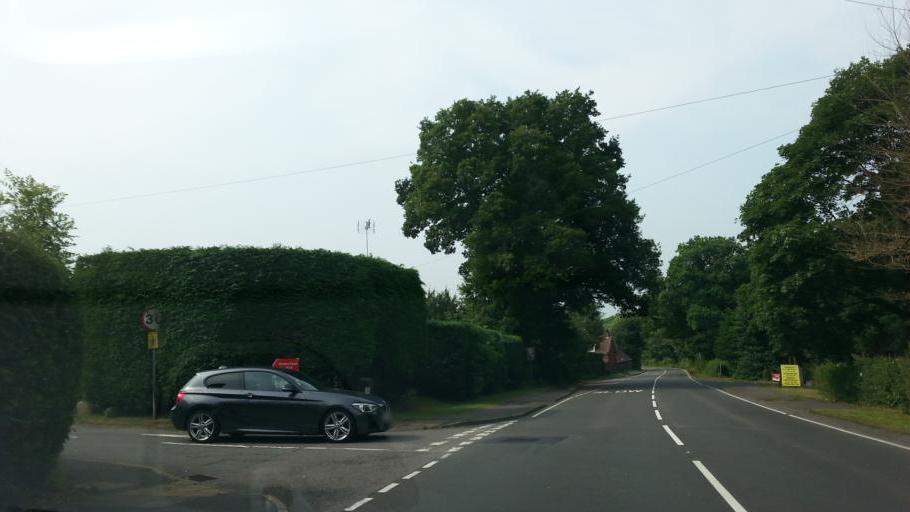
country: GB
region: England
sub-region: Warwickshire
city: Studley
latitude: 52.2919
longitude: -1.8838
